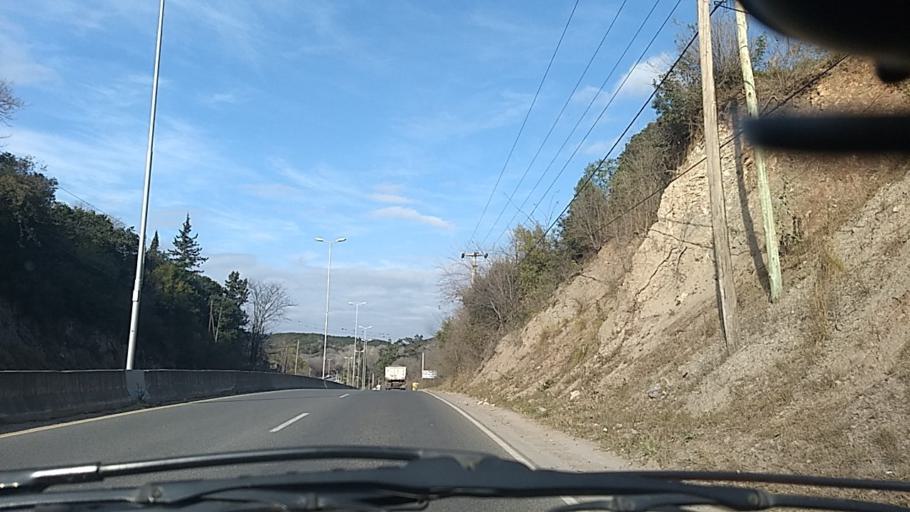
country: AR
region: Cordoba
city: Salsipuedes
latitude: -31.1504
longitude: -64.2988
